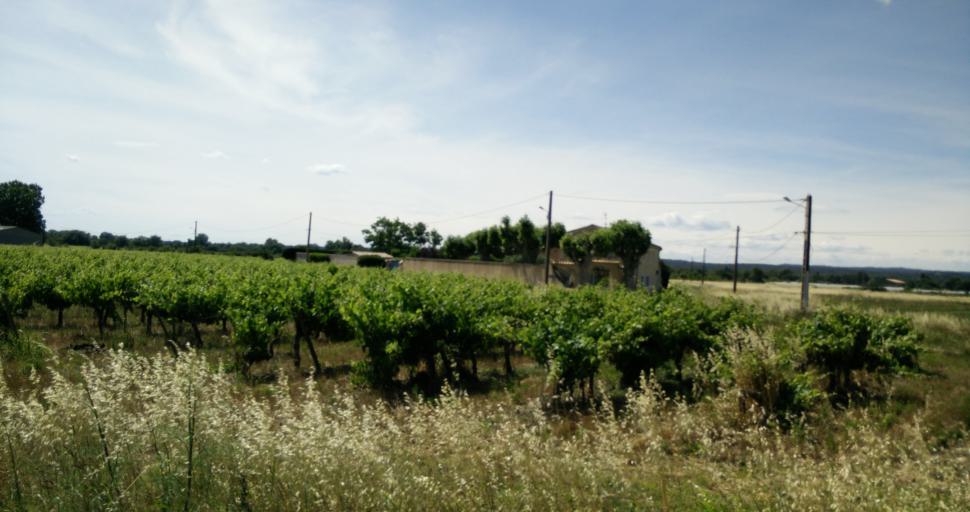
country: FR
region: Languedoc-Roussillon
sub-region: Departement du Gard
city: Aubord
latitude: 43.7561
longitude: 4.3098
